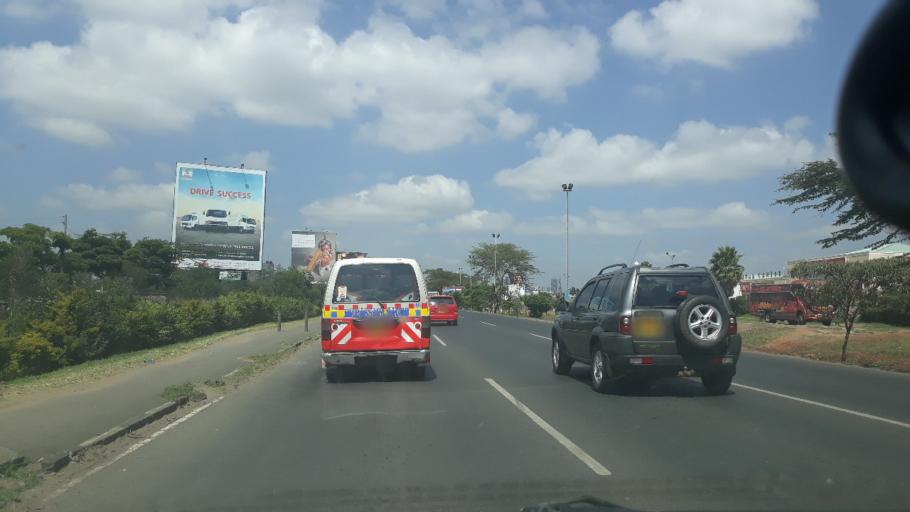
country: KE
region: Nairobi Area
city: Pumwani
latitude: -1.3182
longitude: 36.8356
